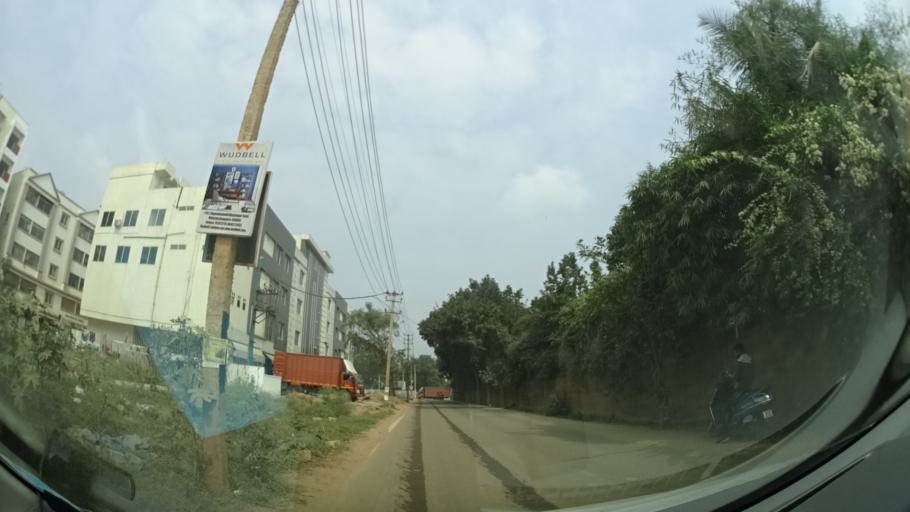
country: IN
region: Karnataka
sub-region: Bangalore Rural
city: Hoskote
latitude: 12.9815
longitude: 77.7579
